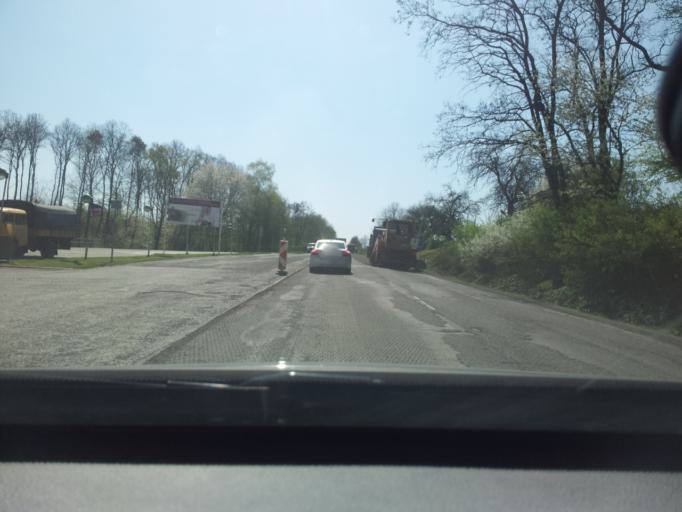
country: SK
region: Nitriansky
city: Banovce nad Bebravou
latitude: 48.7731
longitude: 18.1815
